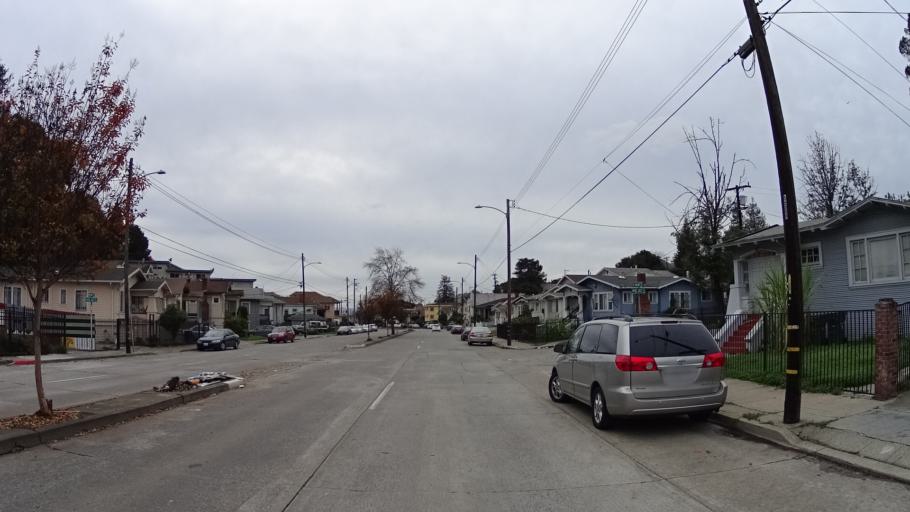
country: US
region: California
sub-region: Alameda County
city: Piedmont
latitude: 37.7951
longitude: -122.2377
